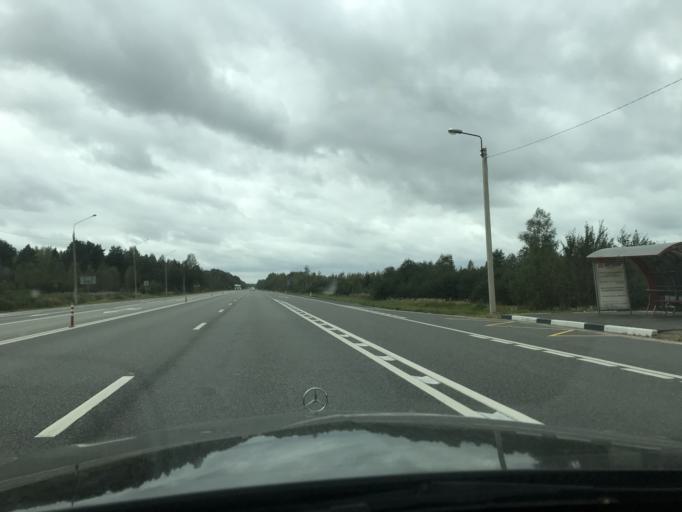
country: RU
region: Smolensk
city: Golynki
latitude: 54.7199
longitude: 31.2785
